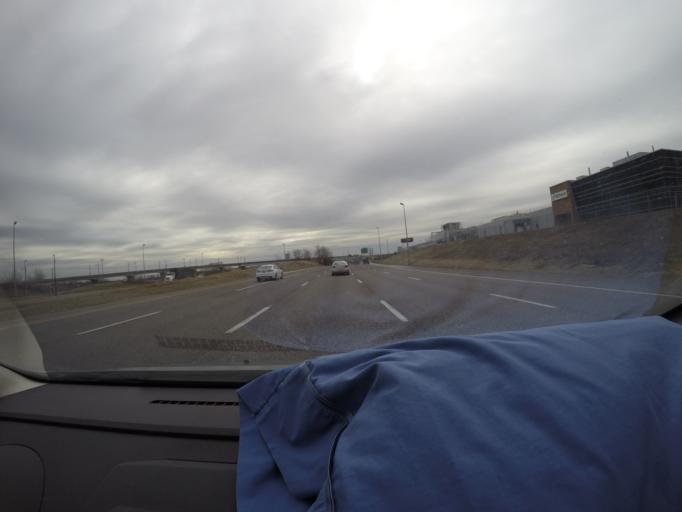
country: US
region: Missouri
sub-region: Saint Louis County
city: Saint Johns
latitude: 38.7316
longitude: -90.3382
